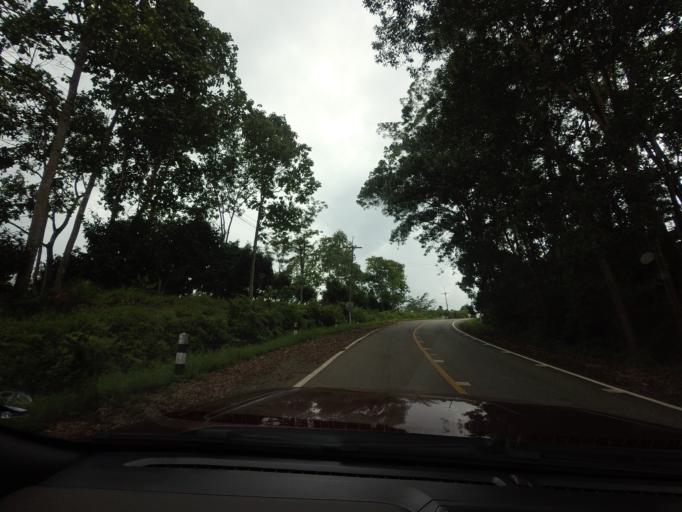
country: TH
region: Narathiwat
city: Sukhirin
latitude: 5.9787
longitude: 101.7026
